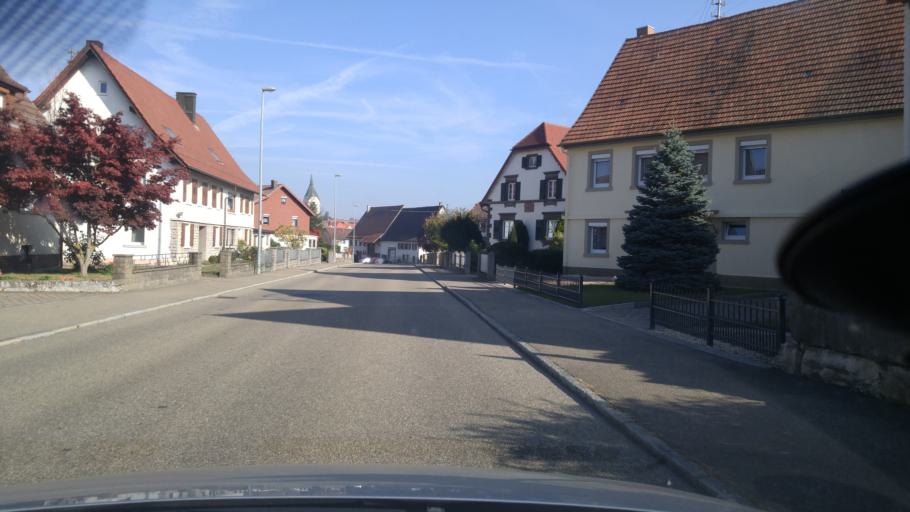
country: DE
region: Baden-Wuerttemberg
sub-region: Karlsruhe Region
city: Empfingen
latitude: 48.3892
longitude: 8.7056
